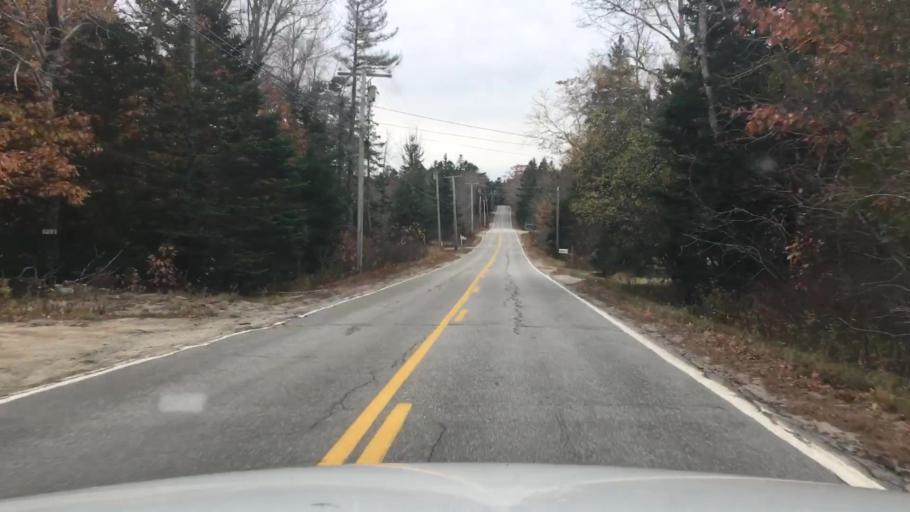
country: US
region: Maine
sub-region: Hancock County
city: Sedgwick
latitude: 44.3383
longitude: -68.5628
